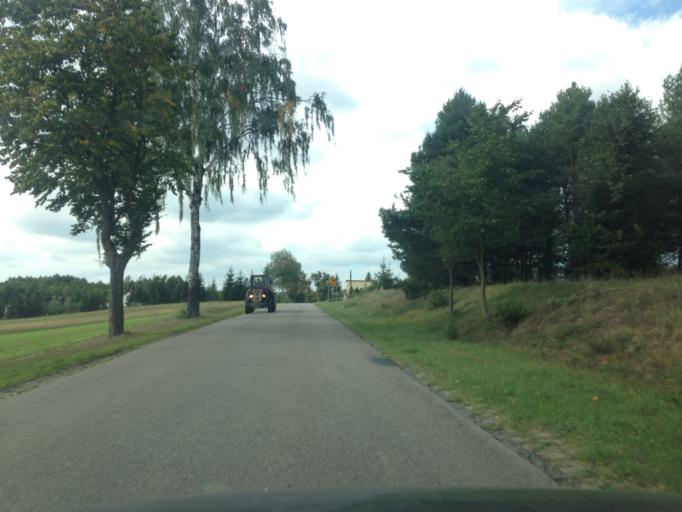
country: PL
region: Kujawsko-Pomorskie
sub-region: Powiat brodnicki
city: Bartniczka
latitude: 53.2395
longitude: 19.6197
